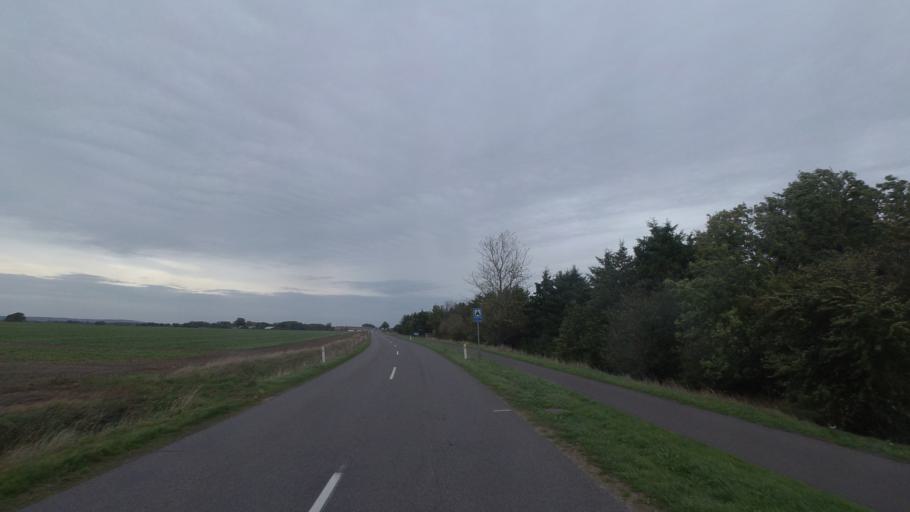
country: DK
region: Capital Region
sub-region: Bornholm Kommune
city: Nexo
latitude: 55.0069
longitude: 15.0911
